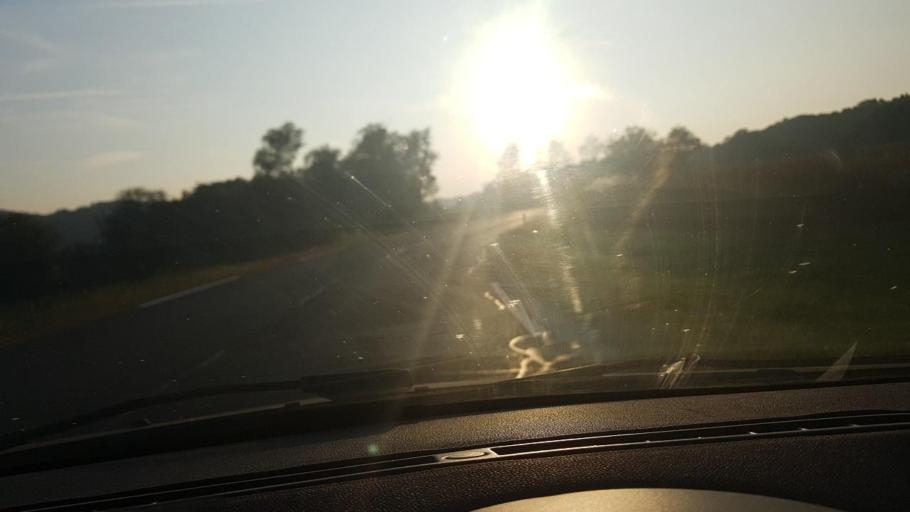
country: SI
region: Majsperk
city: Majsperk
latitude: 46.3365
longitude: 15.7083
